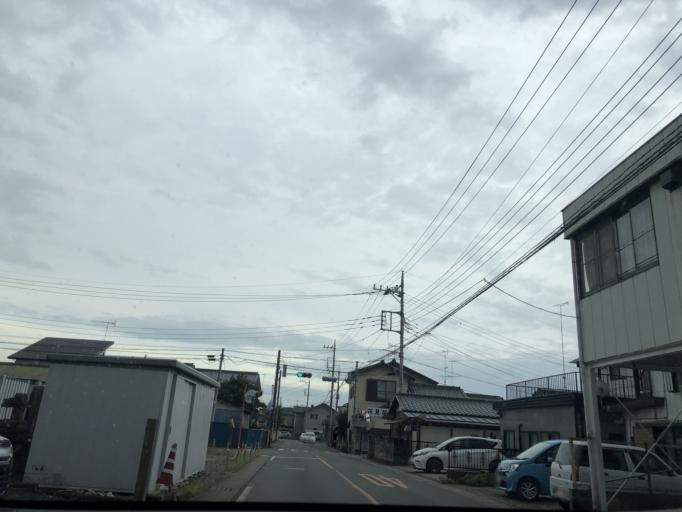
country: JP
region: Tochigi
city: Sano
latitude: 36.3074
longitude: 139.5710
